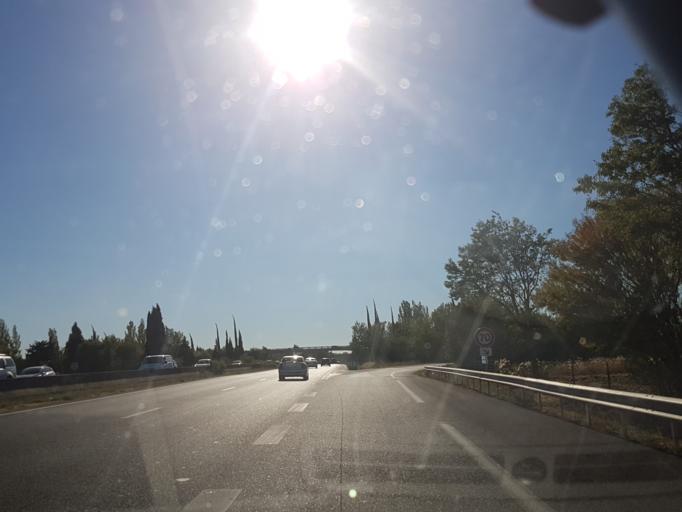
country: FR
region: Provence-Alpes-Cote d'Azur
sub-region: Departement du Vaucluse
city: Entraigues-sur-la-Sorgue
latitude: 43.9938
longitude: 4.9278
